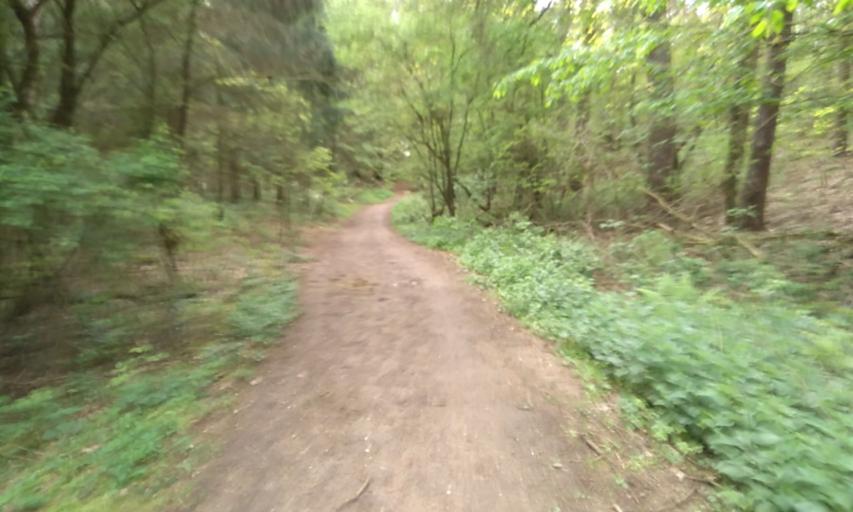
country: DE
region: Lower Saxony
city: Buxtehude
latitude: 53.4498
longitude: 9.6775
